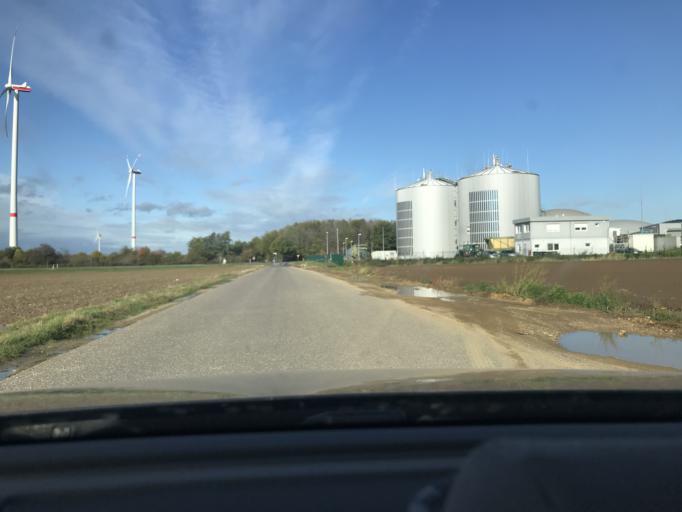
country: DE
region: North Rhine-Westphalia
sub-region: Regierungsbezirk Koln
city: Elsdorf
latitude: 50.9551
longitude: 6.5930
